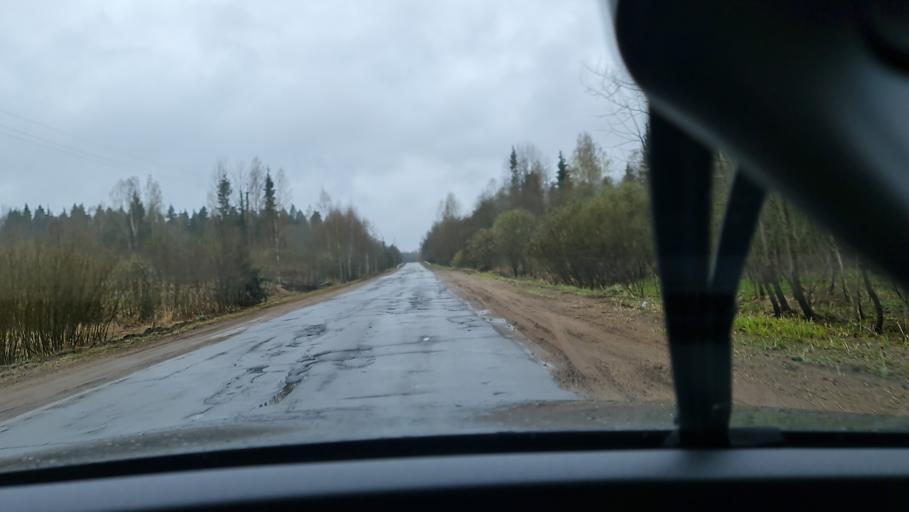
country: RU
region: Novgorod
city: Kresttsy
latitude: 58.0347
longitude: 32.8425
